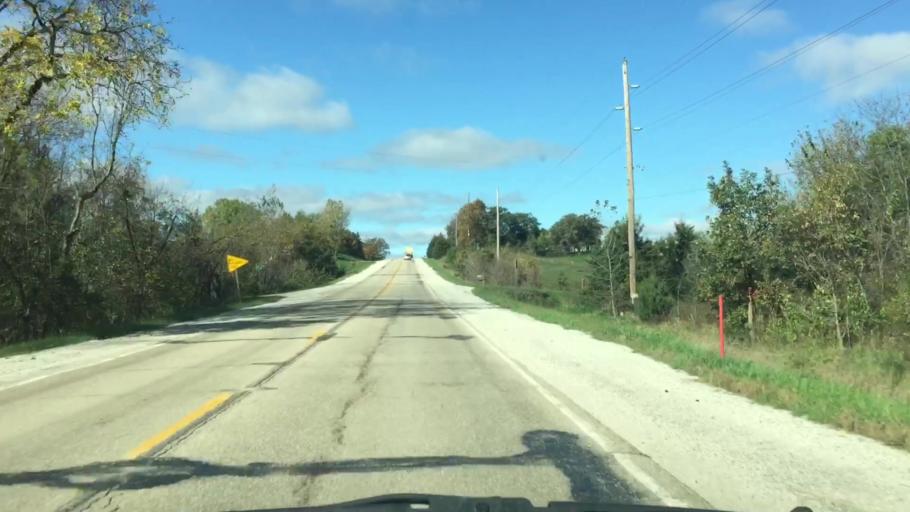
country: US
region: Iowa
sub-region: Decatur County
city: Leon
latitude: 40.7414
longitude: -93.7903
